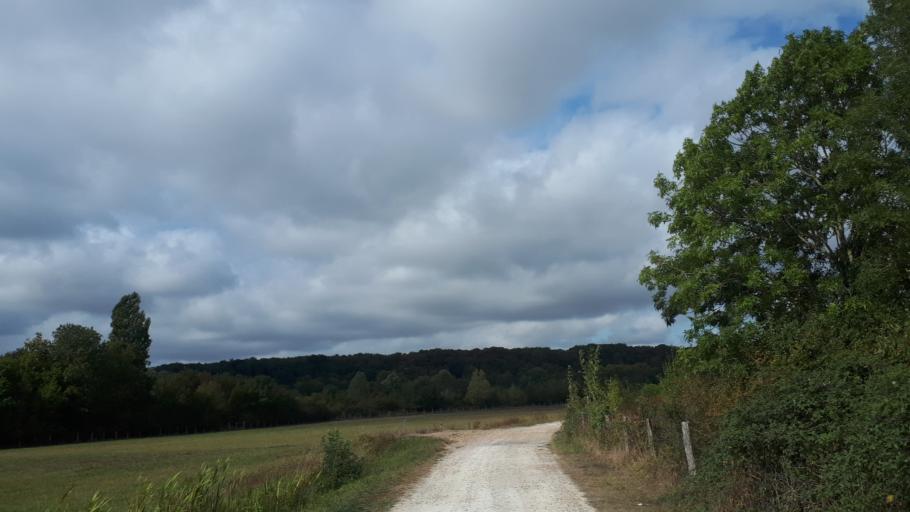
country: FR
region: Centre
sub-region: Departement du Loir-et-Cher
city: Villiers-sur-Loir
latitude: 47.7882
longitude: 0.9929
